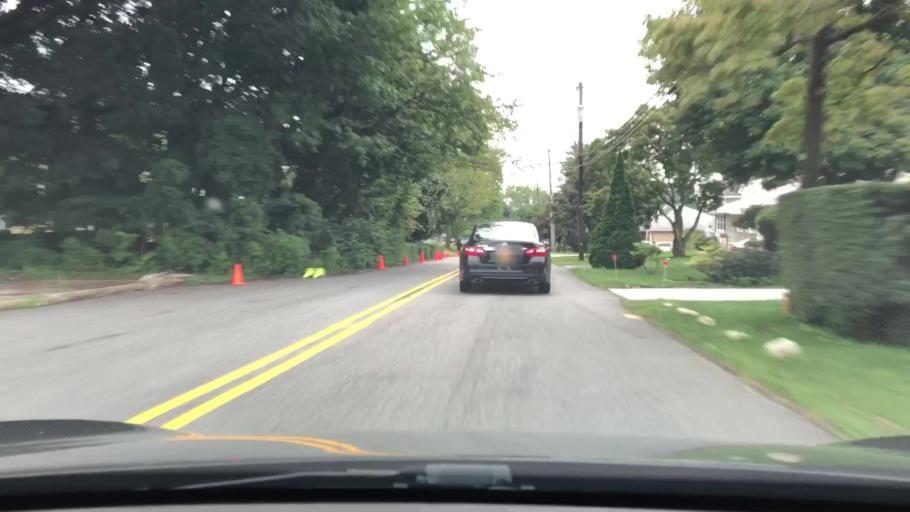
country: US
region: Pennsylvania
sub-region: Delaware County
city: Broomall
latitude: 39.9839
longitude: -75.3583
